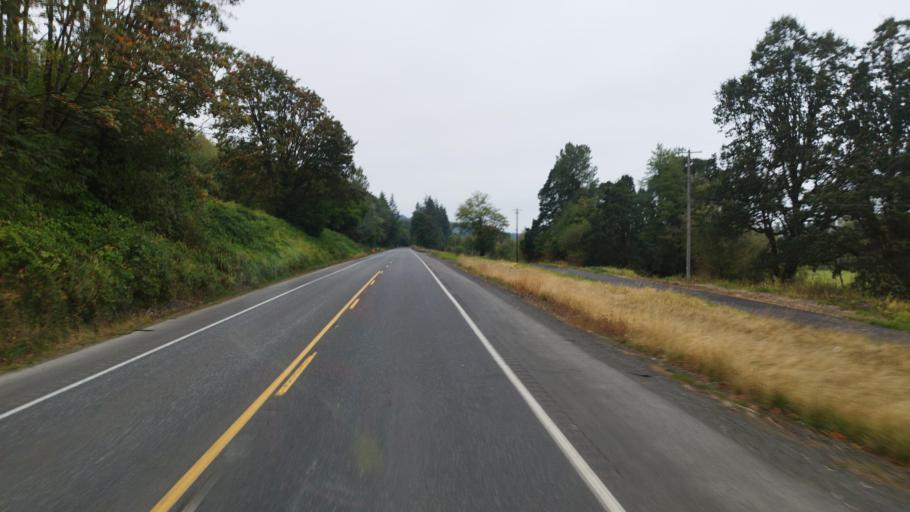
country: US
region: Washington
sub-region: Cowlitz County
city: Kalama
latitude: 45.9460
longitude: -122.8607
